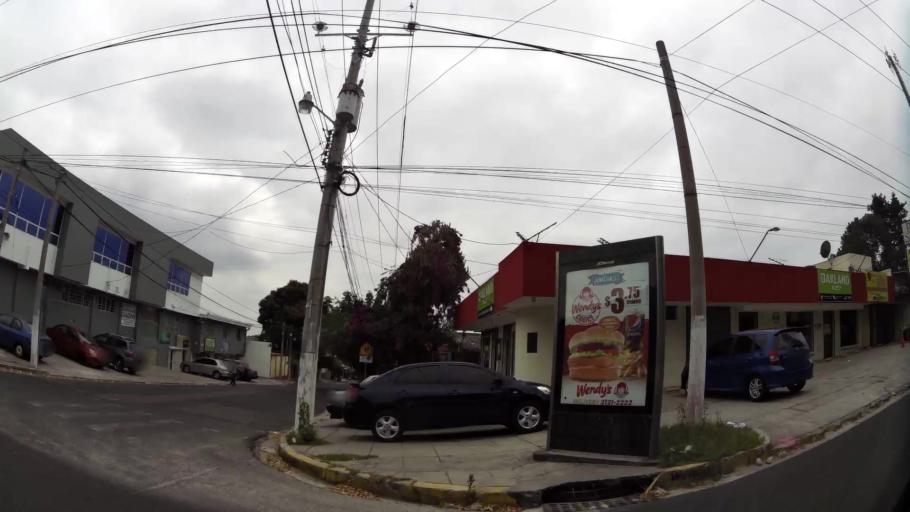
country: SV
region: San Salvador
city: Mejicanos
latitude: 13.7054
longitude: -89.2357
